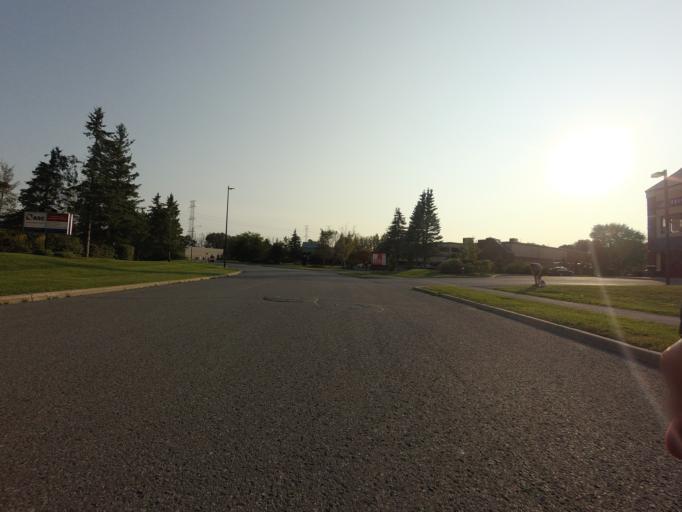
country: CA
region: Ontario
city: Bells Corners
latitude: 45.2859
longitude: -75.8747
